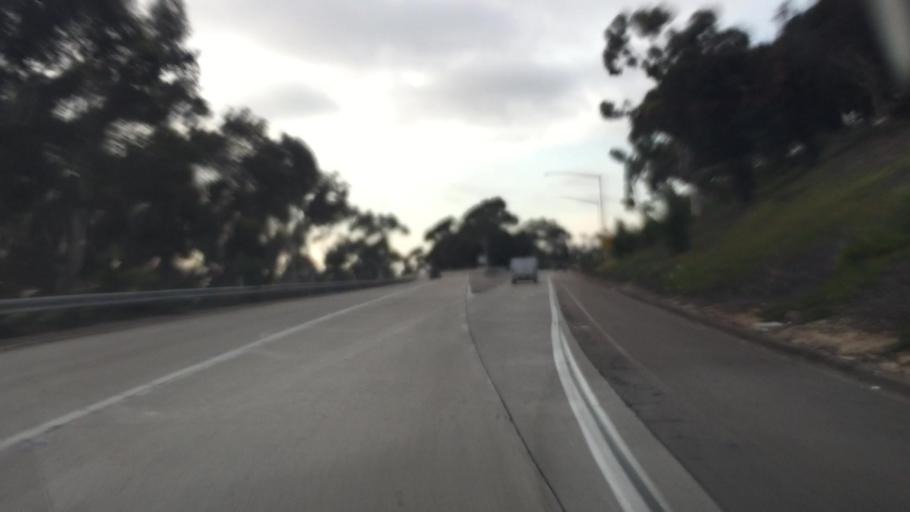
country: US
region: California
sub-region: San Diego County
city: National City
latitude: 32.7155
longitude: -117.1022
